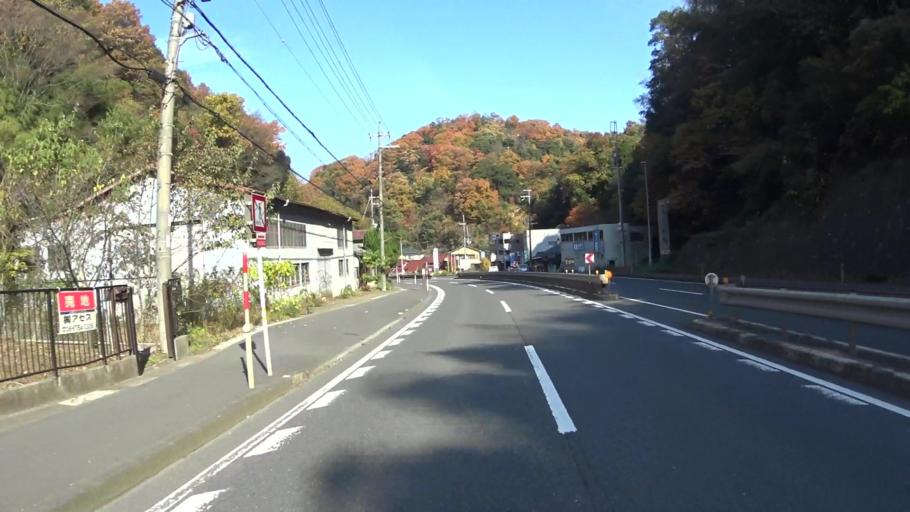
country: JP
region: Kyoto
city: Maizuru
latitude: 35.4631
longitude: 135.3626
